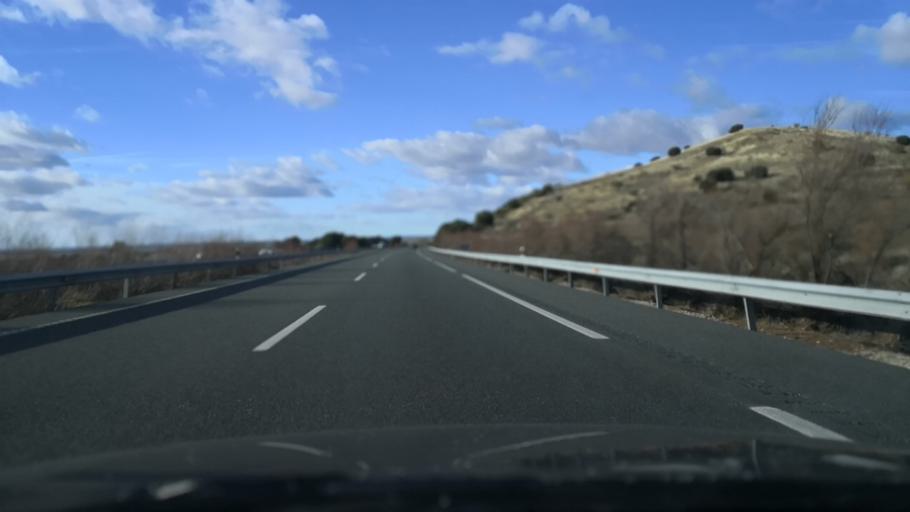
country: ES
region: Castille and Leon
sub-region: Provincia de Segovia
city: Labajos
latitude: 40.8385
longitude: -4.5337
